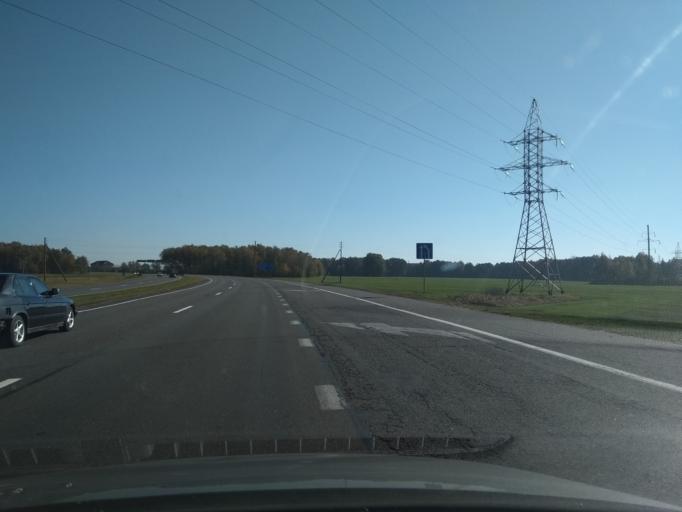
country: BY
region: Brest
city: Kobryn
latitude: 52.1790
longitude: 24.3351
